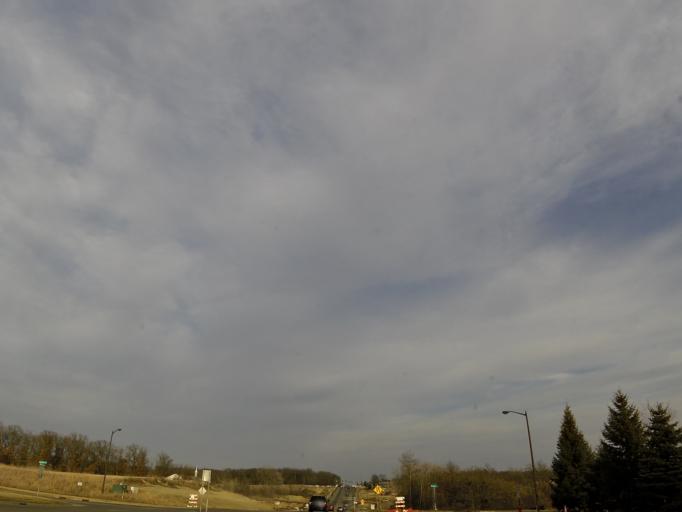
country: US
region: Minnesota
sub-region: Dakota County
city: Lakeville
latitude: 44.6812
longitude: -93.2861
